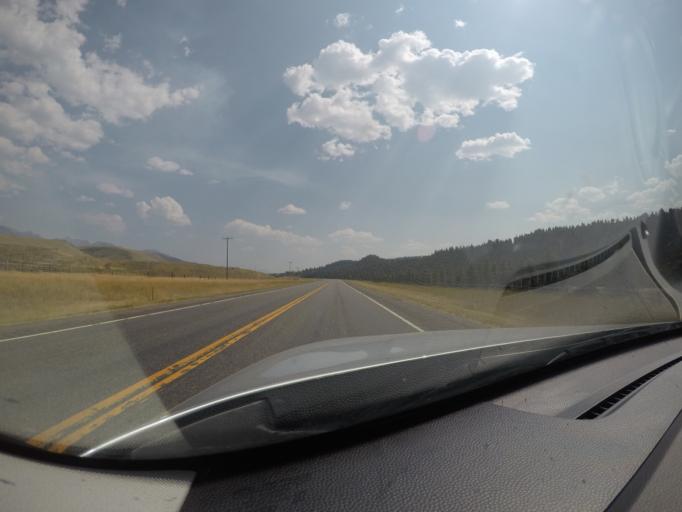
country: US
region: Montana
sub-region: Gallatin County
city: Big Sky
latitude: 44.9722
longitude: -111.6436
